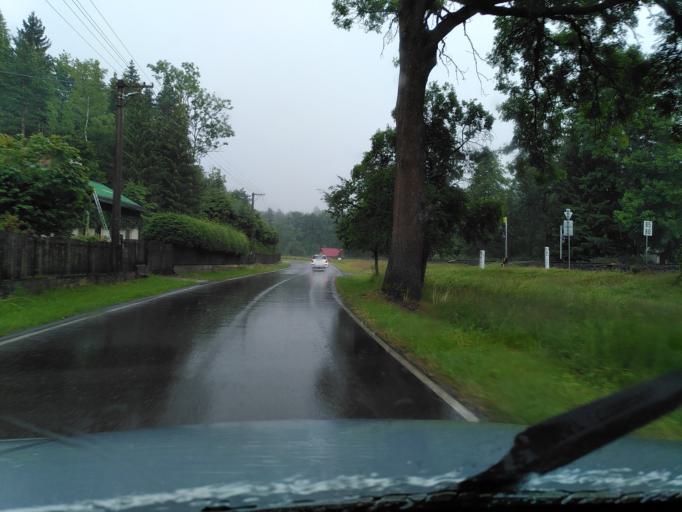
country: CZ
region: Ustecky
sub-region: Okres Decin
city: Chribska
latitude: 50.8139
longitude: 14.5109
